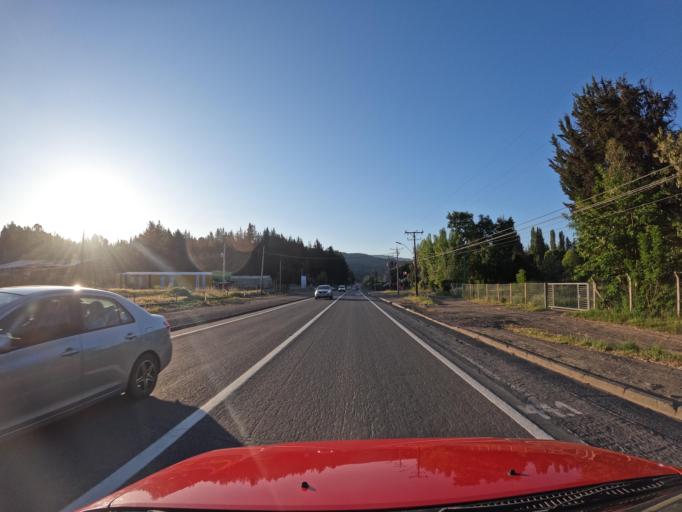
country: CL
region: Biobio
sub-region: Provincia de Concepcion
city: Lota
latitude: -37.1571
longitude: -72.9676
